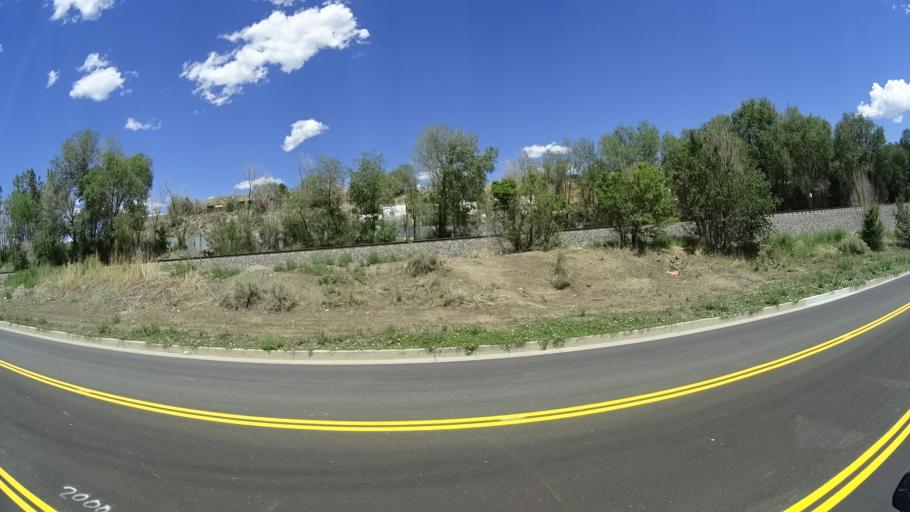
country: US
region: Colorado
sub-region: El Paso County
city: Colorado Springs
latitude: 38.8152
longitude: -104.8096
